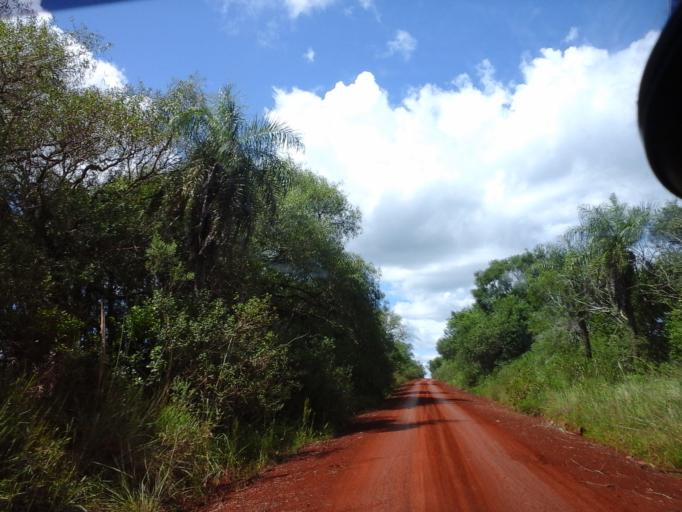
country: AR
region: Misiones
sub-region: Departamento de Apostoles
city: Apostoles
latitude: -27.9789
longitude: -55.7768
